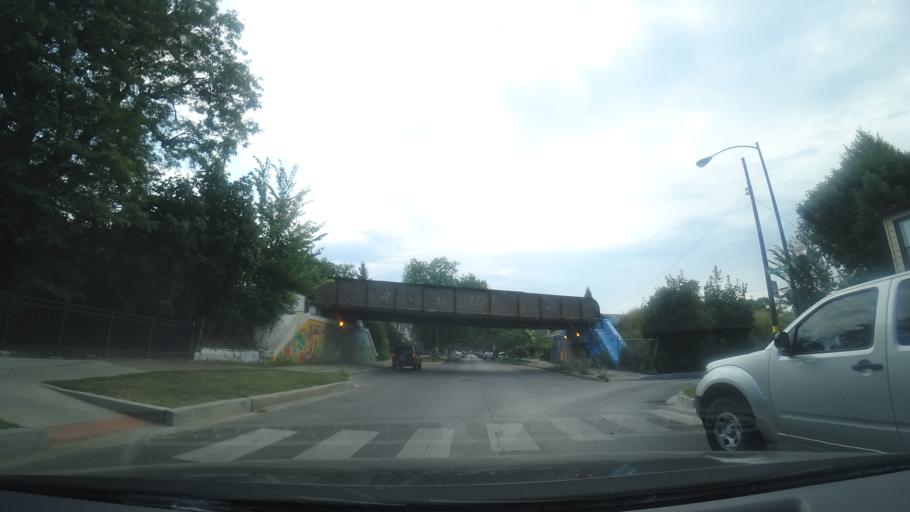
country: US
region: Illinois
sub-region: Cook County
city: Lincolnwood
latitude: 41.9426
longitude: -87.7376
